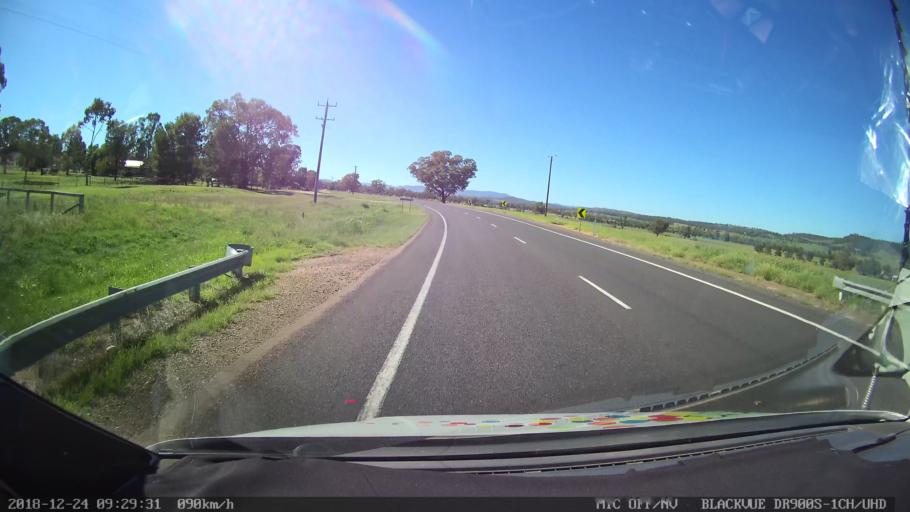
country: AU
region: New South Wales
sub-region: Liverpool Plains
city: Quirindi
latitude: -31.5512
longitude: 150.6920
